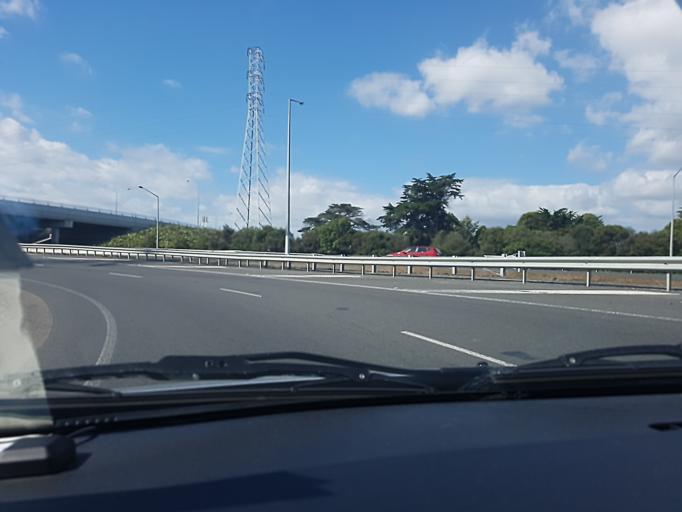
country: NZ
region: Auckland
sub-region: Auckland
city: Papakura
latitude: -37.0746
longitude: 174.9287
